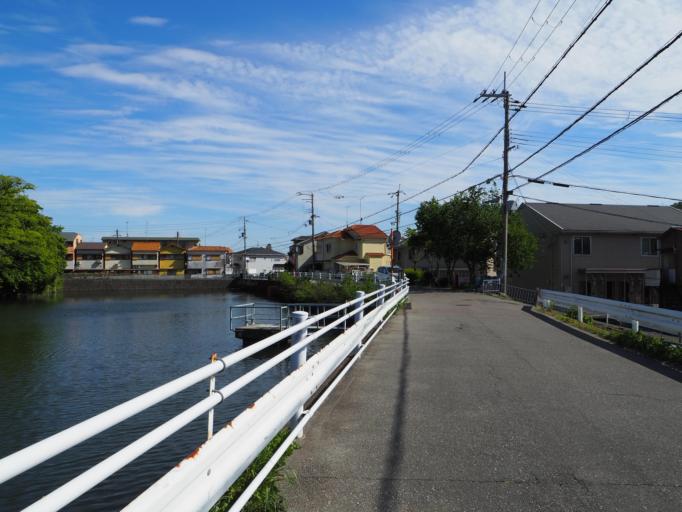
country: JP
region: Hyogo
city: Takarazuka
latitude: 34.8168
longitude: 135.3367
